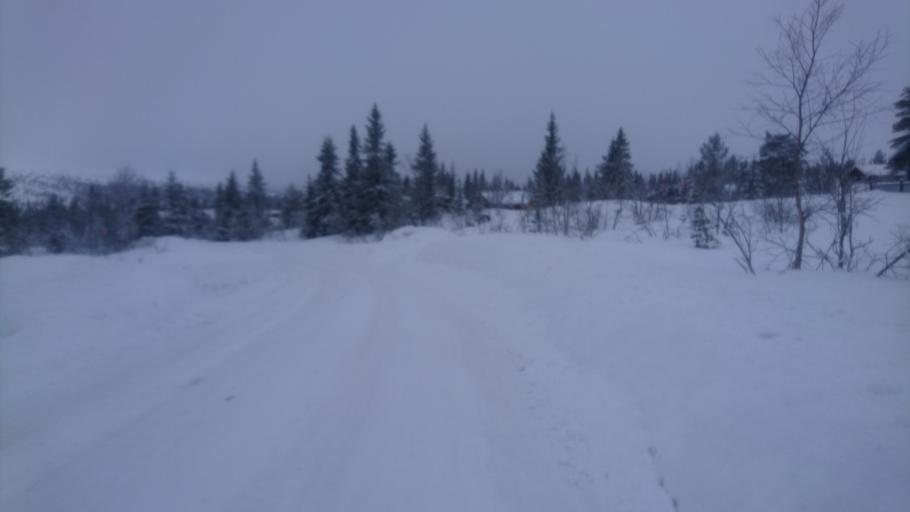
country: SE
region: Dalarna
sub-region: Malung-Saelens kommun
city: Malung
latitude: 61.1651
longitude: 13.1086
